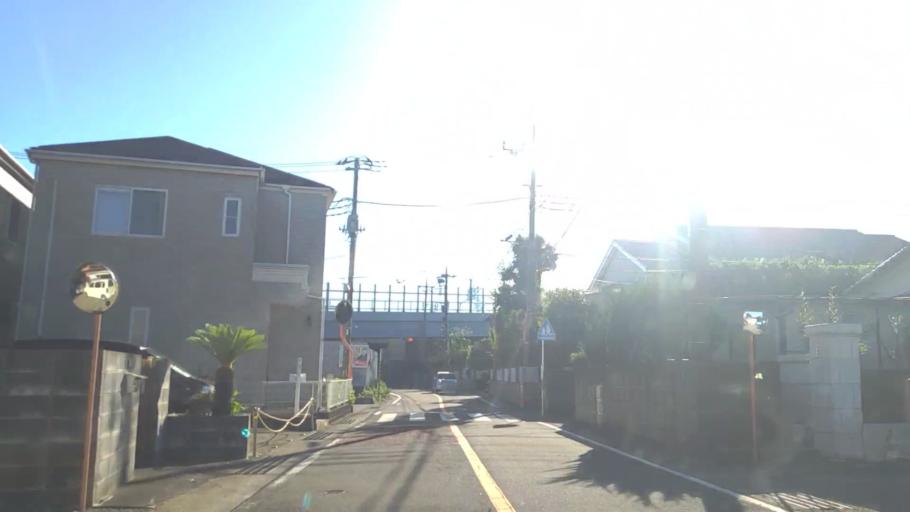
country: JP
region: Kanagawa
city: Atsugi
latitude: 35.4241
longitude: 139.3678
